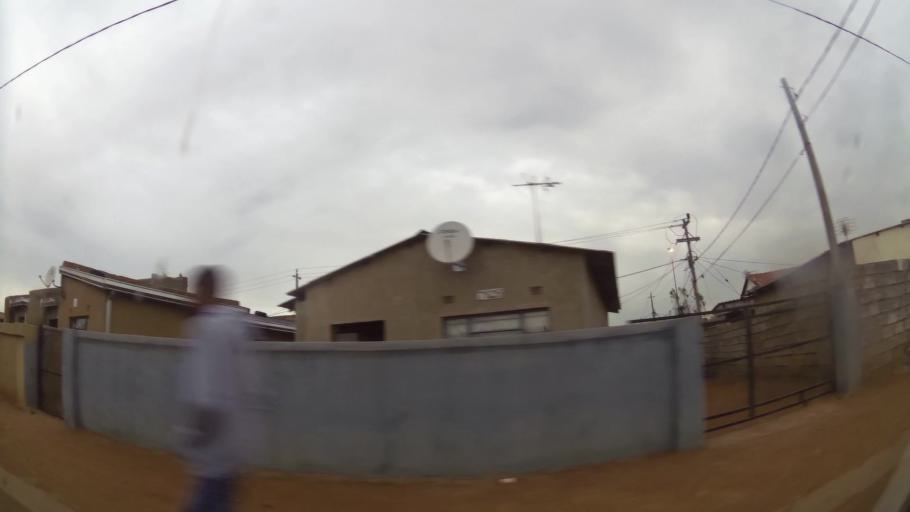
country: ZA
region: Gauteng
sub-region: Ekurhuleni Metropolitan Municipality
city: Germiston
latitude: -26.3805
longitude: 28.1785
